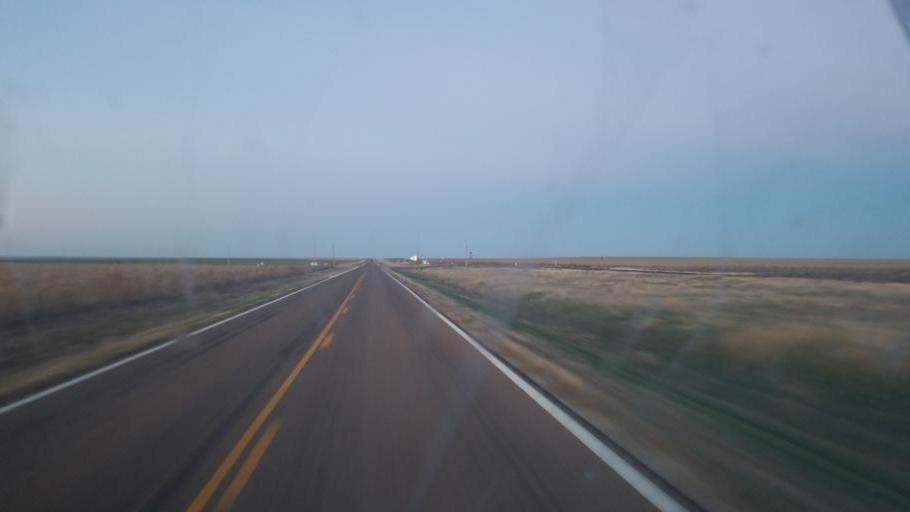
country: US
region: Kansas
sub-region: Wallace County
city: Sharon Springs
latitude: 38.9969
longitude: -101.4037
